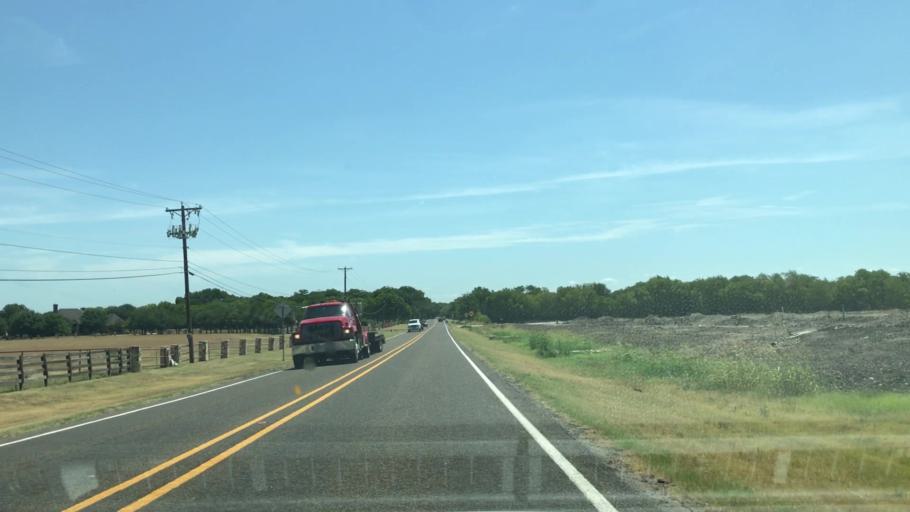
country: US
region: Texas
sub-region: Collin County
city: Fairview
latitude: 33.1566
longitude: -96.6304
